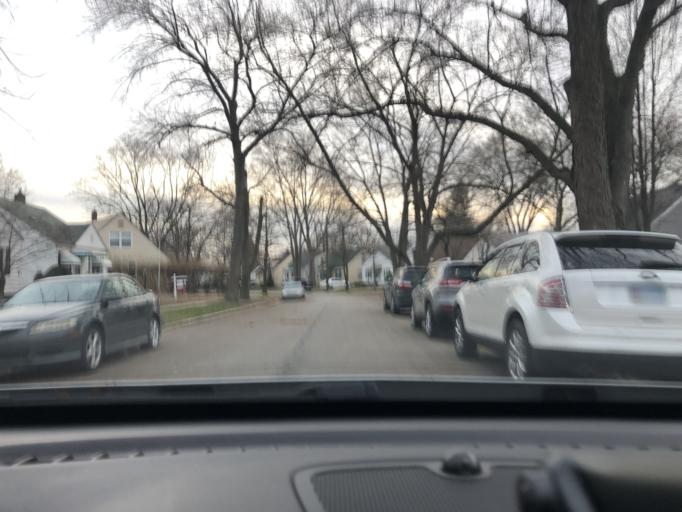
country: US
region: Michigan
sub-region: Wayne County
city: Allen Park
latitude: 42.2877
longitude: -83.2272
